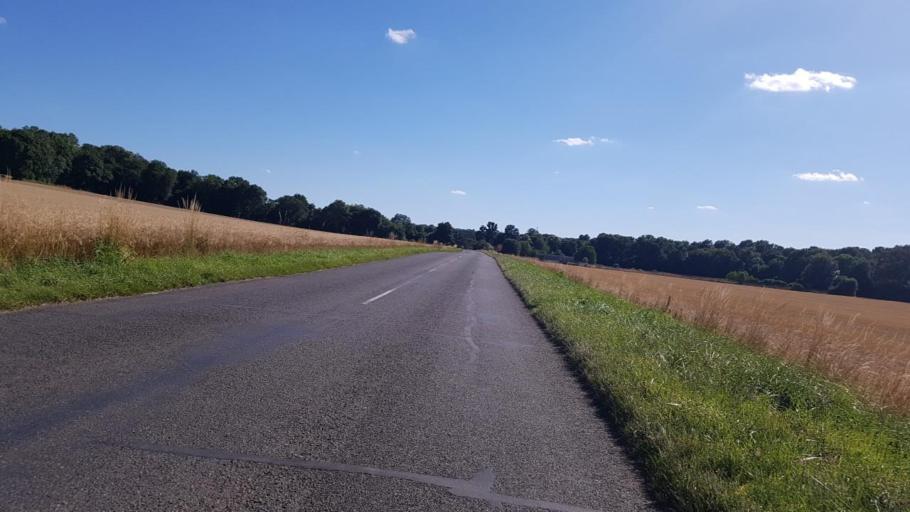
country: FR
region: Ile-de-France
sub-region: Departement de Seine-et-Marne
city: Coupvray
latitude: 48.9139
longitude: 2.7860
